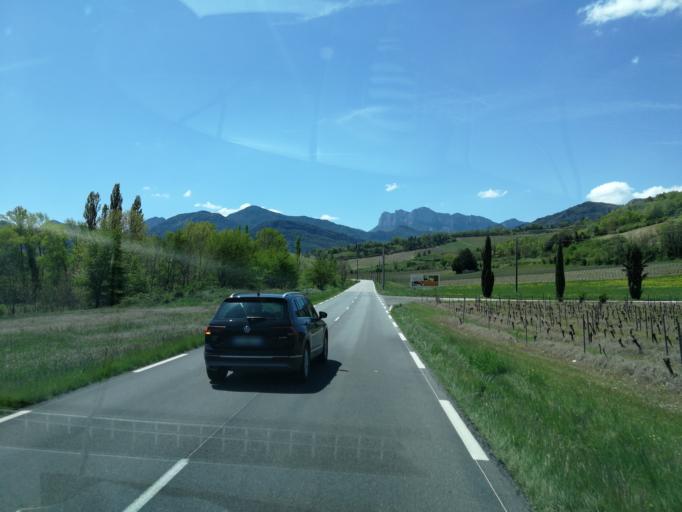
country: FR
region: Rhone-Alpes
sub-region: Departement de la Drome
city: Die
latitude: 44.7231
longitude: 5.2670
